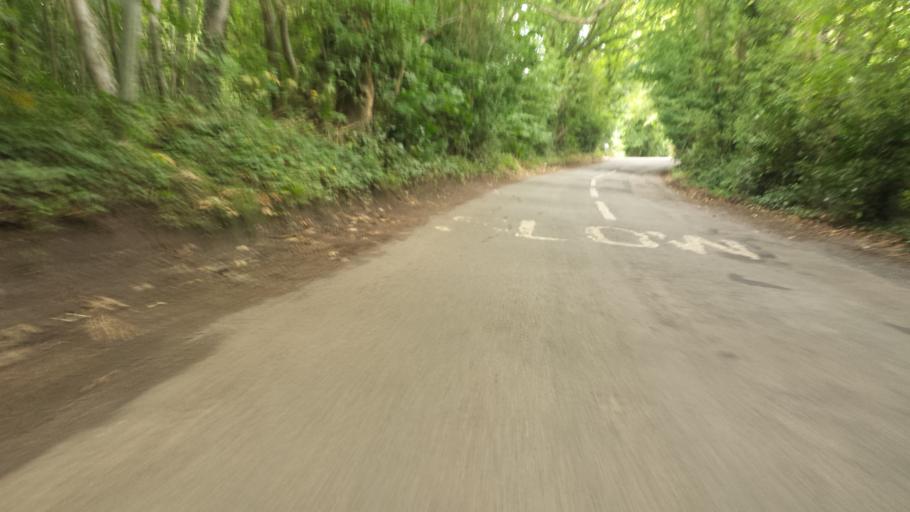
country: GB
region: England
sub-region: Kent
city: Shoreham
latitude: 51.3630
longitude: 0.1529
